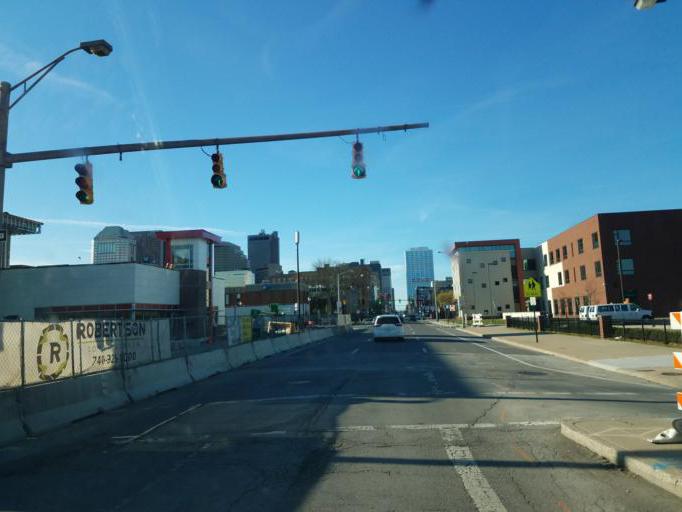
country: US
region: Ohio
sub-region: Franklin County
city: Columbus
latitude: 39.9540
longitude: -82.9946
